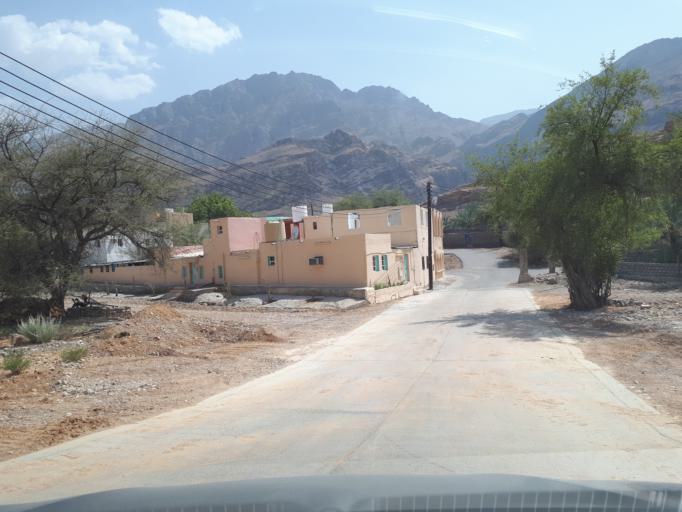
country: OM
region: Ash Sharqiyah
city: Ibra'
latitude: 23.0802
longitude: 58.8720
